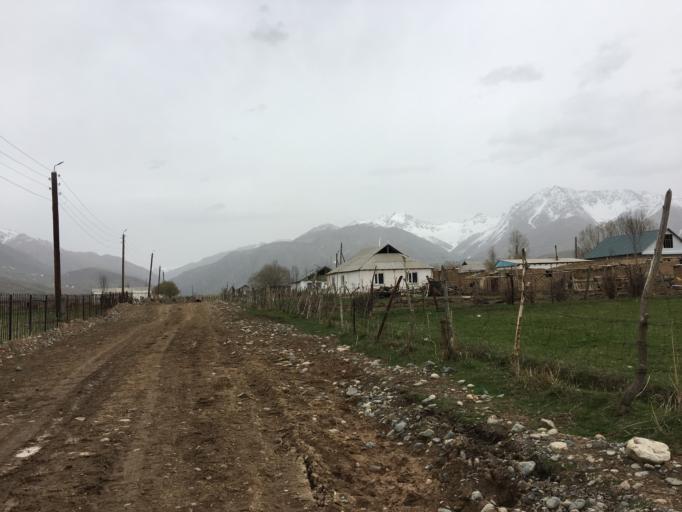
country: KG
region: Naryn
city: Naryn
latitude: 41.5187
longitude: 76.4358
